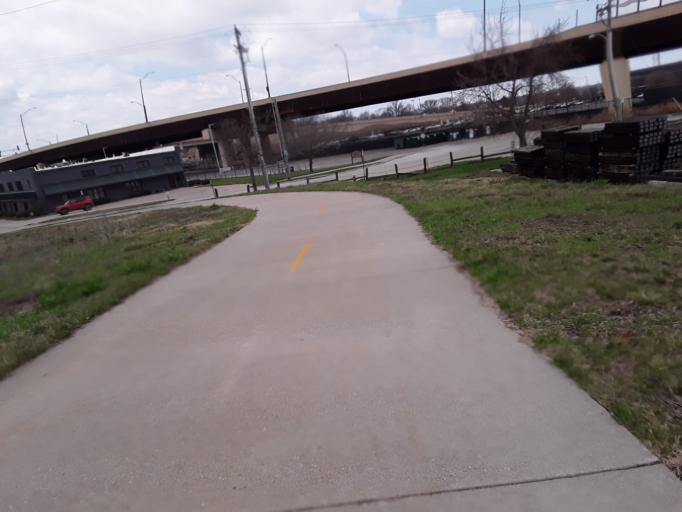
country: US
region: Nebraska
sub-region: Lancaster County
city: Lincoln
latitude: 40.8279
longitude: -96.6958
